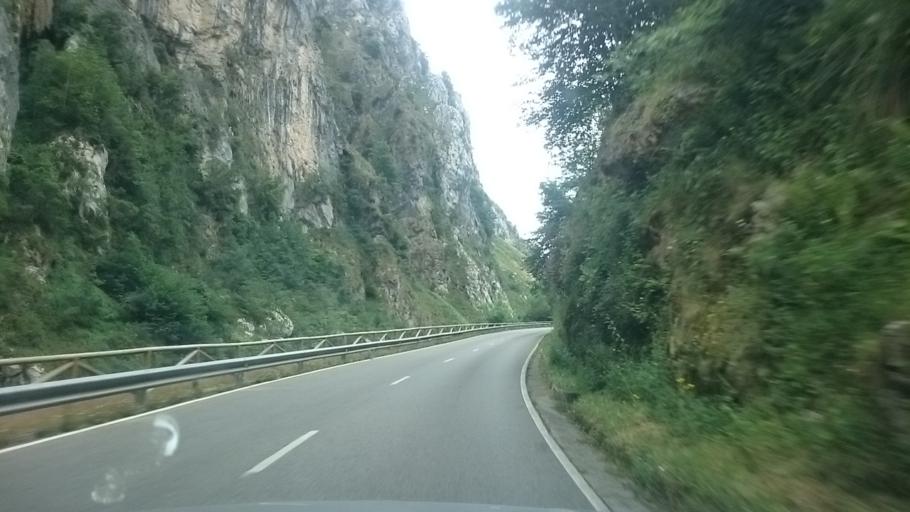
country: ES
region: Asturias
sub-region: Province of Asturias
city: Carrena
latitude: 43.2650
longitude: -4.8320
